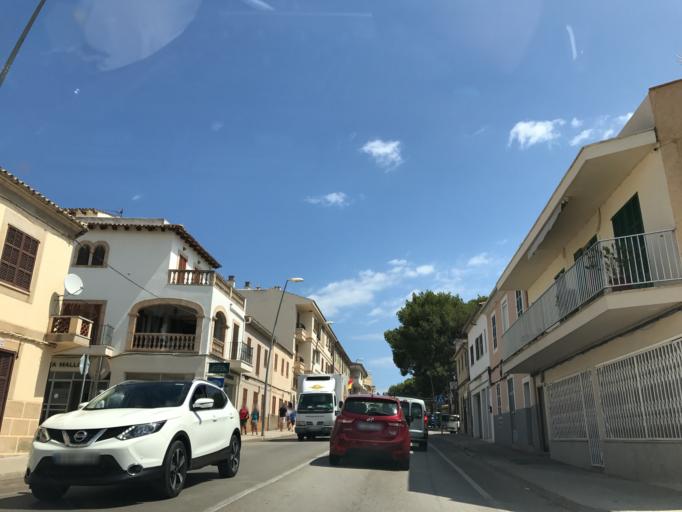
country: ES
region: Balearic Islands
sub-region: Illes Balears
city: Arta
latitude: 39.6905
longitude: 3.3474
